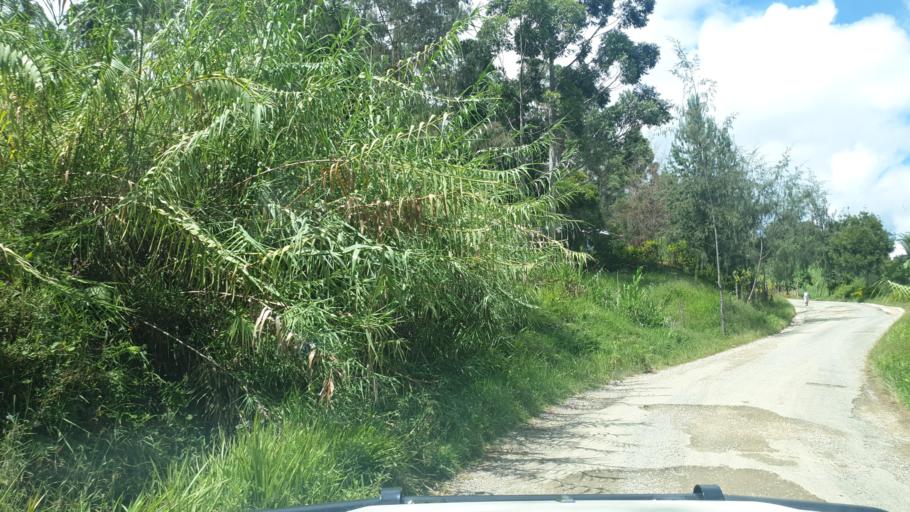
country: PG
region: Chimbu
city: Kundiawa
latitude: -6.1630
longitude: 145.1339
